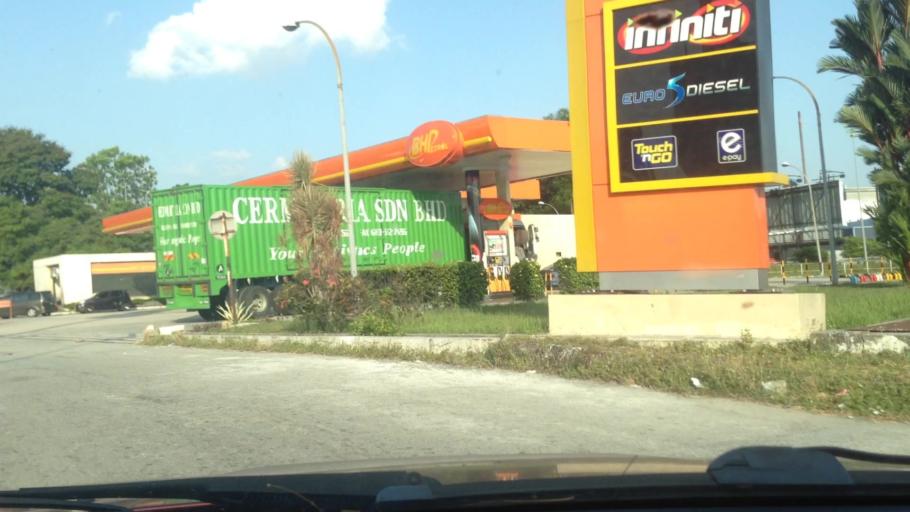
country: MY
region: Selangor
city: Subang Jaya
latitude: 3.0401
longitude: 101.5472
